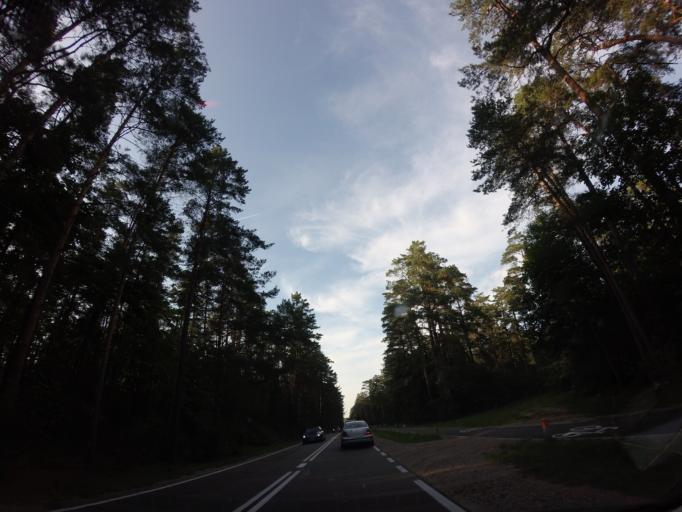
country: PL
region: Podlasie
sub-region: Powiat augustowski
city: Augustow
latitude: 53.8622
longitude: 23.0883
